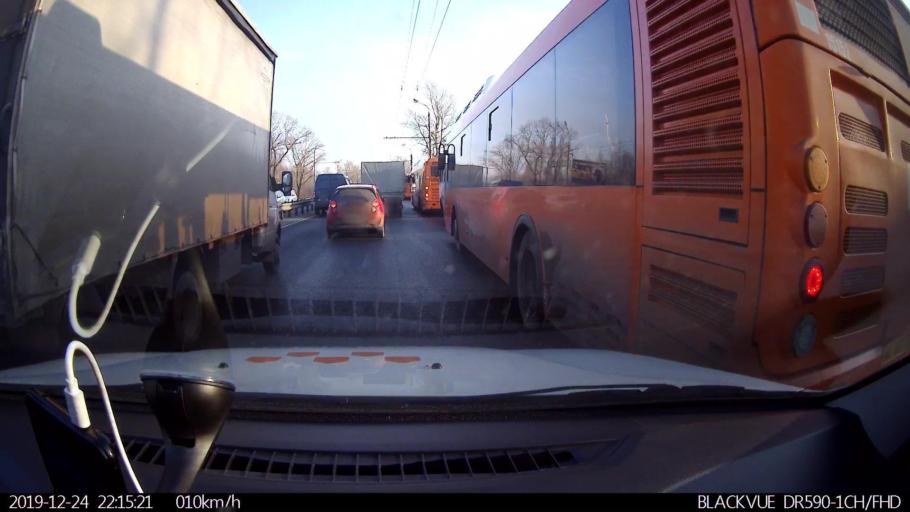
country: RU
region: Nizjnij Novgorod
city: Gorbatovka
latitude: 56.3121
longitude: 43.8323
